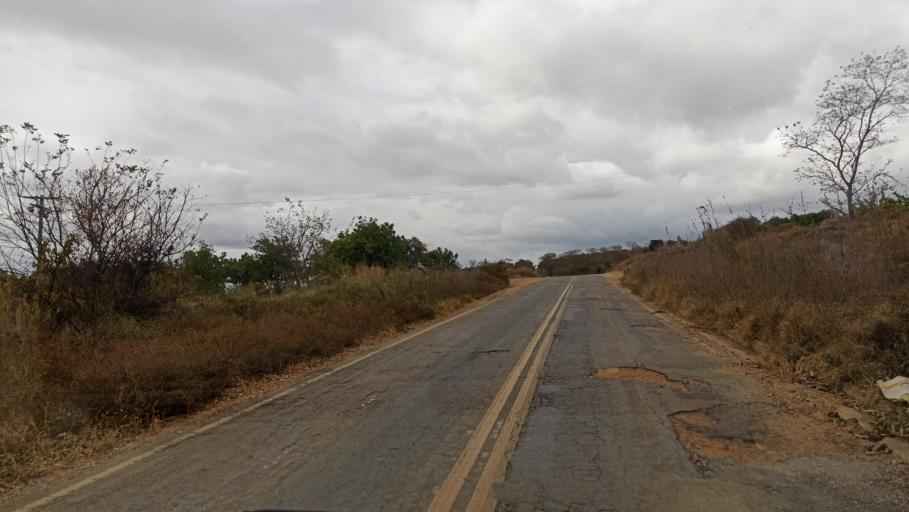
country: BR
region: Minas Gerais
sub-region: Itinga
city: Itinga
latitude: -16.6352
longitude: -41.8034
